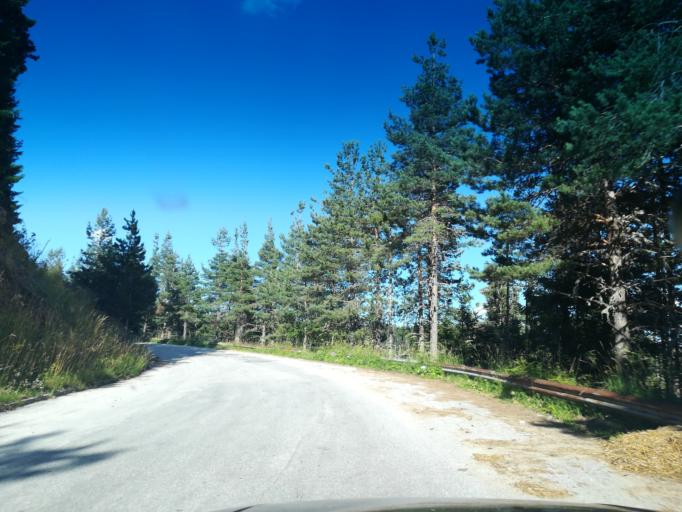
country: BG
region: Smolyan
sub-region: Obshtina Chepelare
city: Chepelare
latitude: 41.6868
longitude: 24.7564
